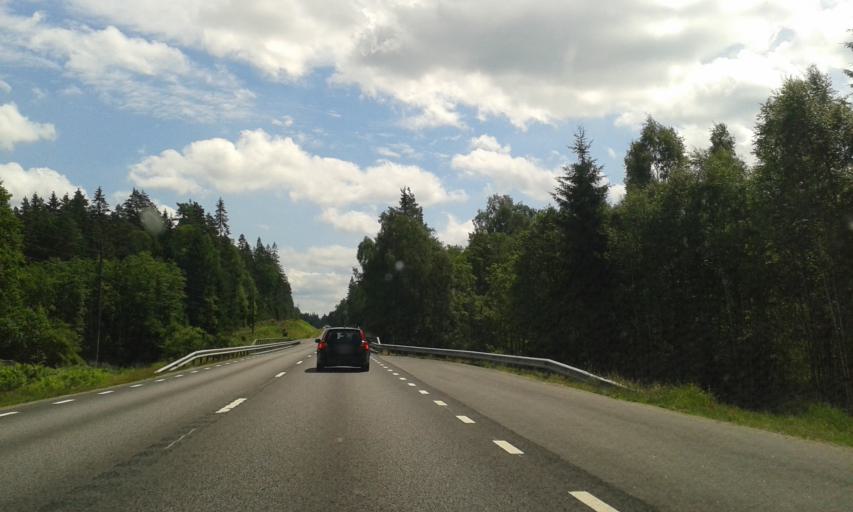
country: SE
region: Joenkoeping
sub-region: Varnamo Kommun
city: Bor
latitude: 57.0585
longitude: 14.2008
